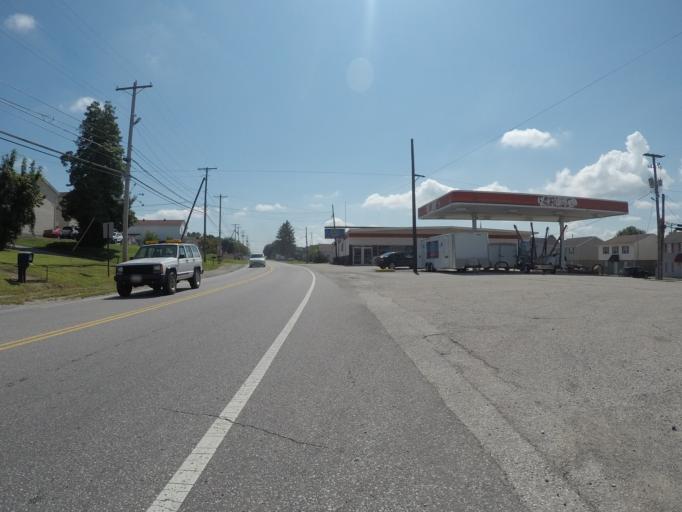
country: US
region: Ohio
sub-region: Lawrence County
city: South Point
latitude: 38.4192
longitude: -82.5879
